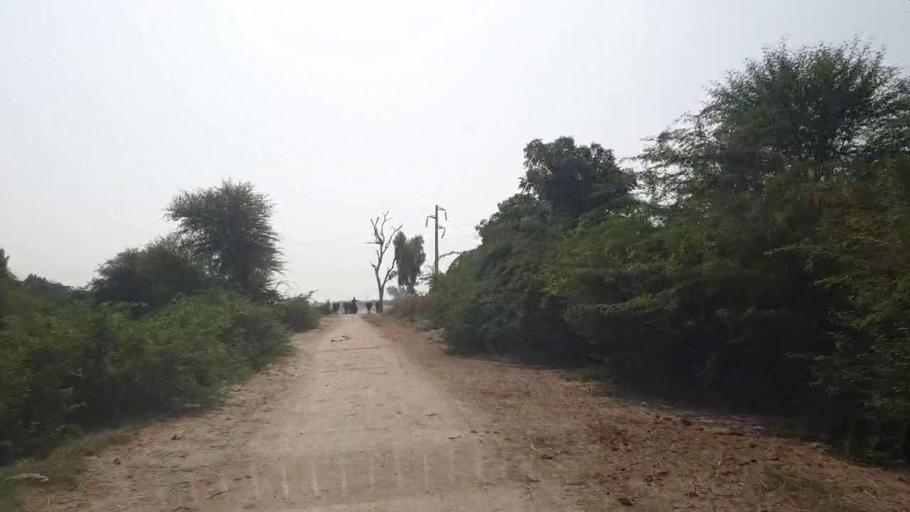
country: PK
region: Sindh
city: Badin
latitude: 24.6379
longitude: 68.8499
